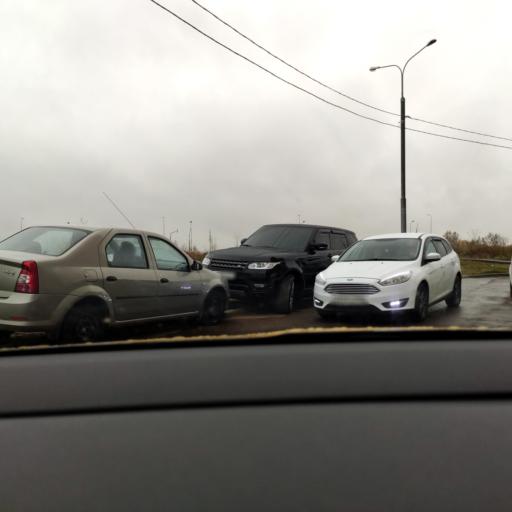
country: RU
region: Moskovskaya
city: Shcherbinka
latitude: 55.5048
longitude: 37.5338
